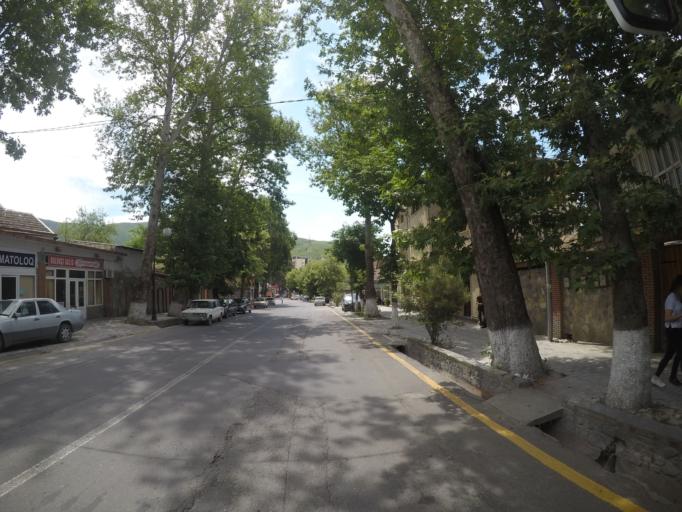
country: AZ
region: Shaki City
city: Sheki
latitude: 41.2047
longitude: 47.1777
